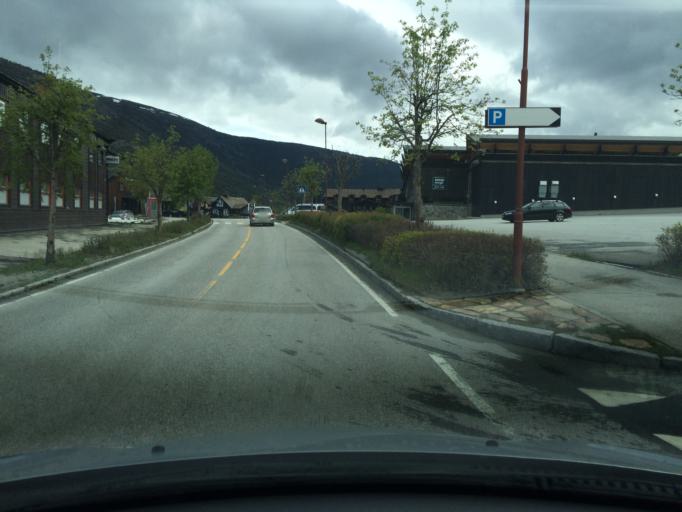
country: NO
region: Oppland
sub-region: Lom
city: Fossbergom
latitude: 61.8366
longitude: 8.5669
